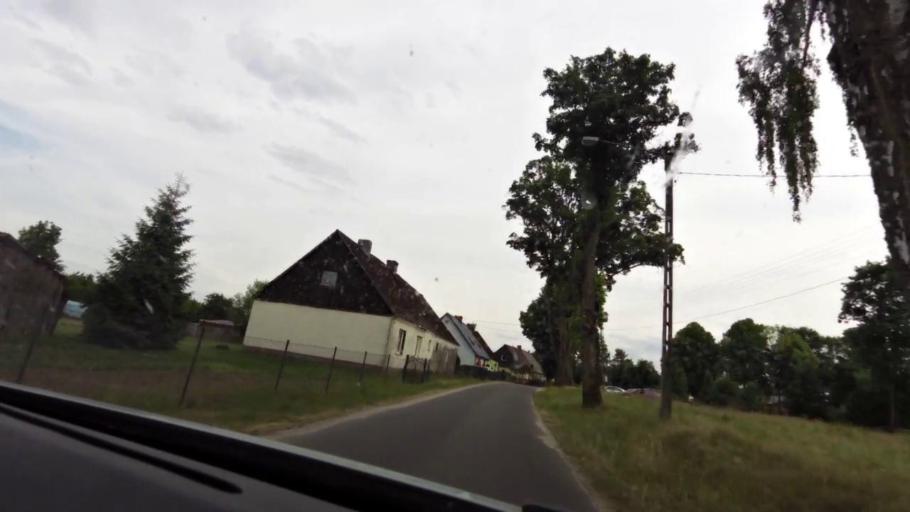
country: PL
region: Pomeranian Voivodeship
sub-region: Powiat bytowski
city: Trzebielino
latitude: 54.2606
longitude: 17.0108
